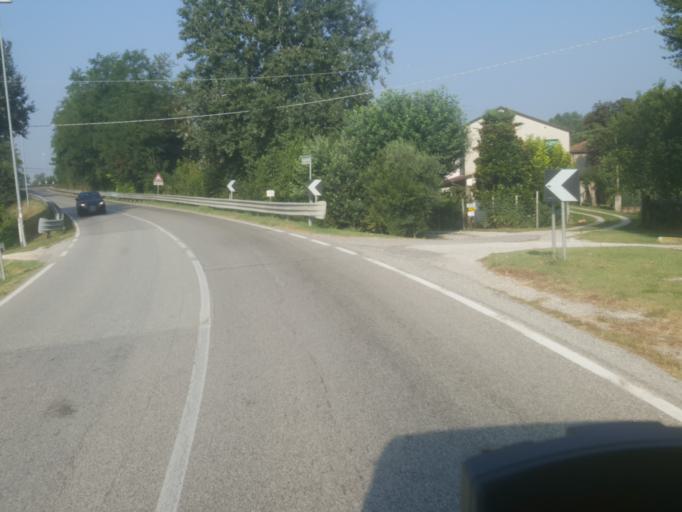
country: IT
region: Emilia-Romagna
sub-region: Provincia di Ravenna
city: Voltana
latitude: 44.5541
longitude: 11.9384
